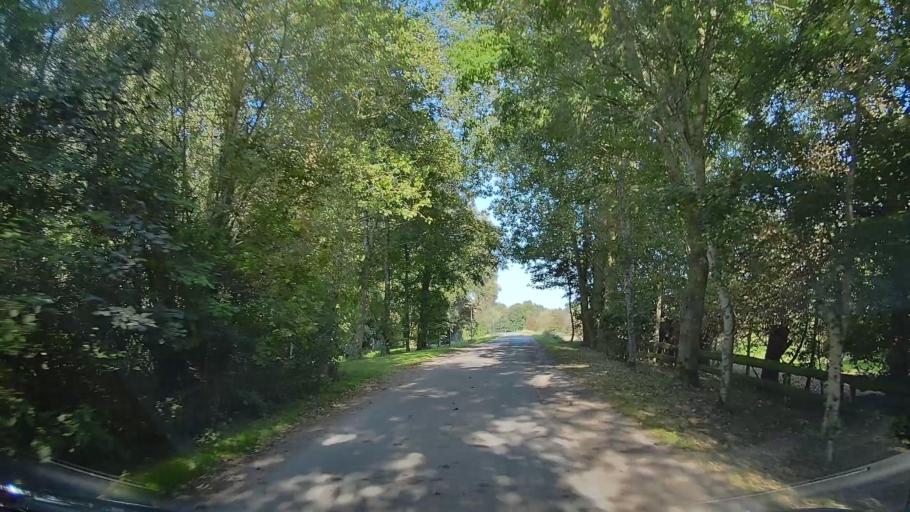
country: DE
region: Lower Saxony
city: Padingbuttel
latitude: 53.7230
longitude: 8.5260
